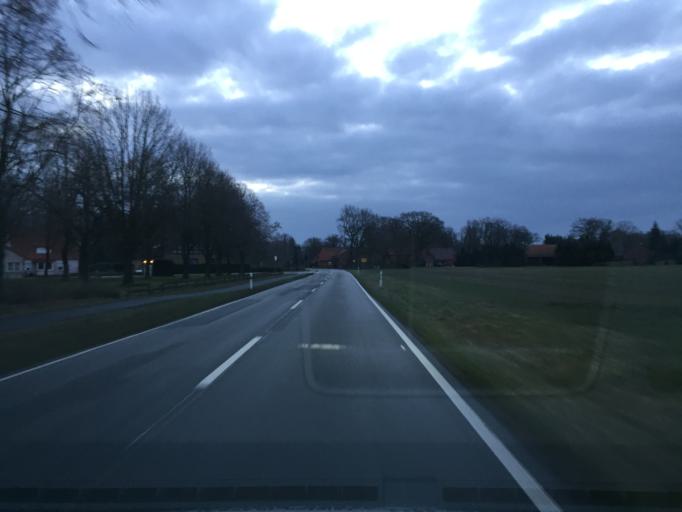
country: DE
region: Lower Saxony
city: Steyerberg
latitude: 52.5957
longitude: 8.9667
